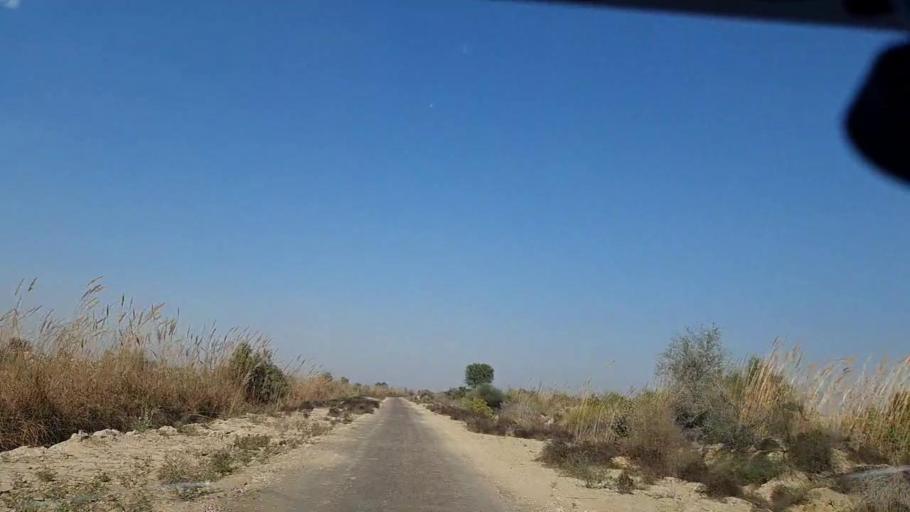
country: PK
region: Sindh
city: Khanpur
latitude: 27.5891
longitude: 69.3757
